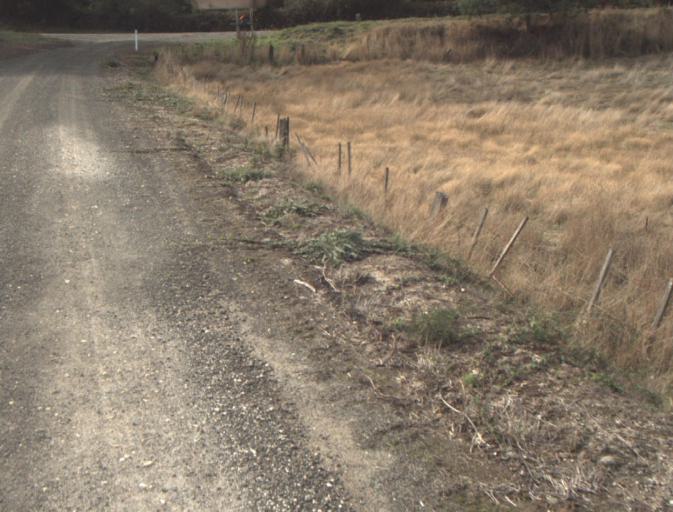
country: AU
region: Tasmania
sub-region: Launceston
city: Mayfield
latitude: -41.1947
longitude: 147.1952
